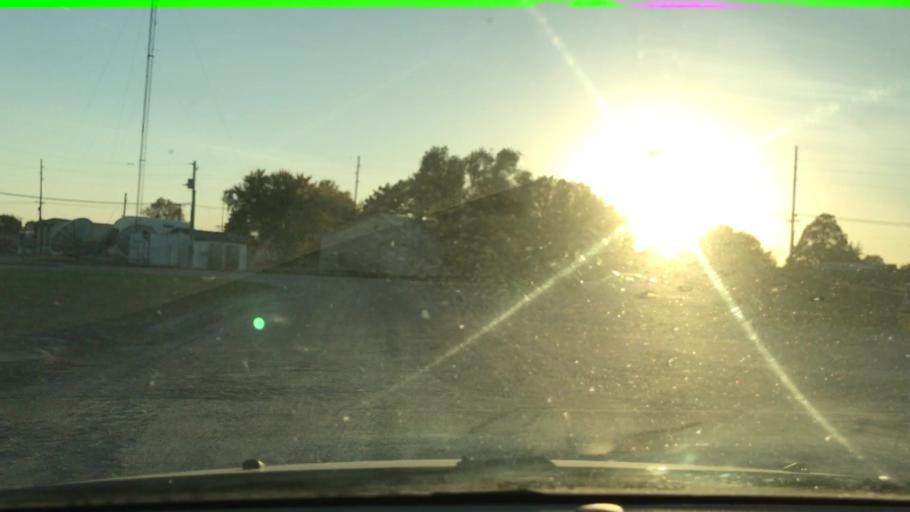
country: US
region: Nebraska
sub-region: Merrick County
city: Central City
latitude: 41.1107
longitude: -98.0091
